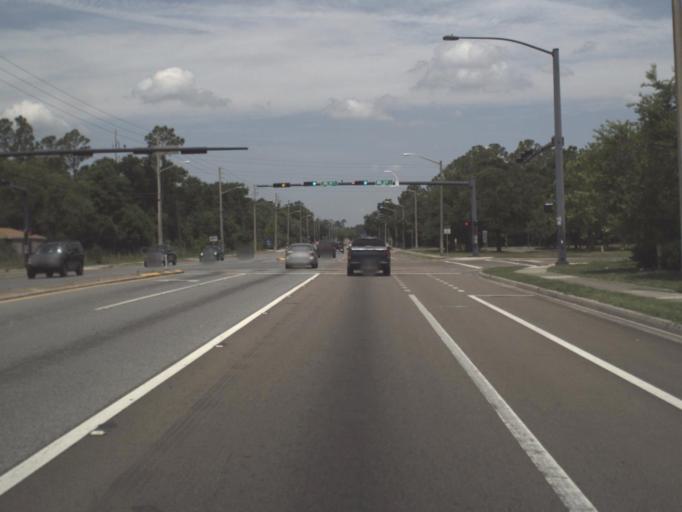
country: US
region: Florida
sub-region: Alachua County
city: Gainesville
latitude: 29.6452
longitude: -82.2937
